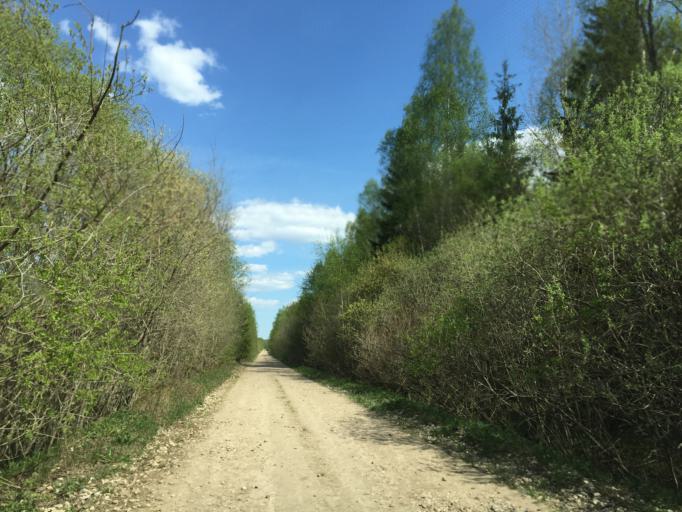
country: LV
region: Limbazu Rajons
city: Limbazi
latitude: 57.4045
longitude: 24.6040
